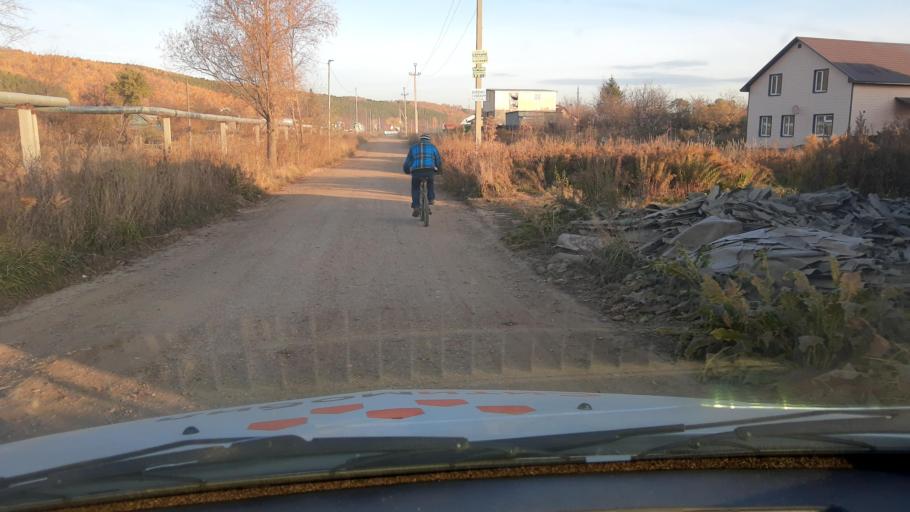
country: RU
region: Bashkortostan
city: Ufa
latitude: 54.8152
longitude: 56.1543
